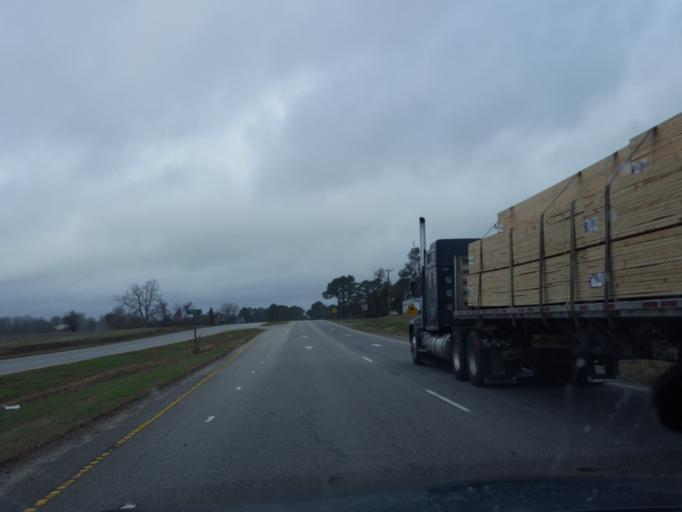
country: US
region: North Carolina
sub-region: Washington County
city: Plymouth
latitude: 35.8300
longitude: -76.7913
